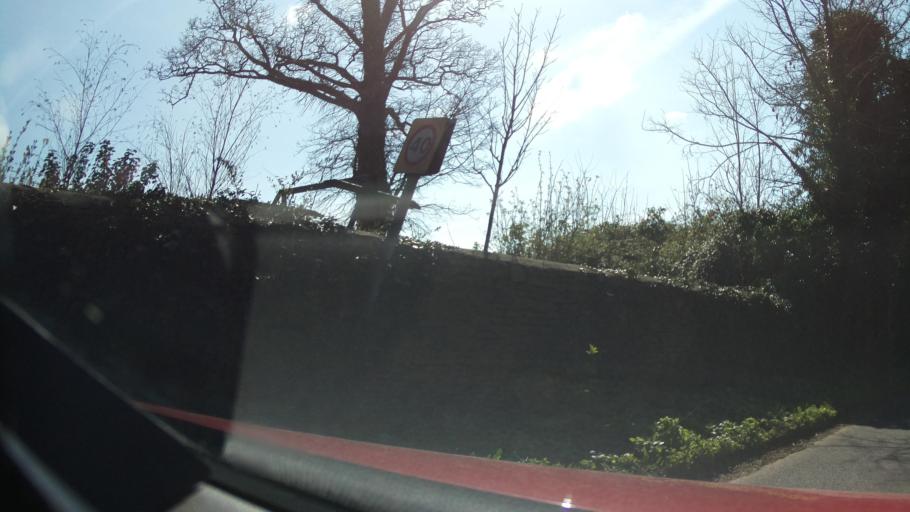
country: GB
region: England
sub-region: Wiltshire
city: Bradford-on-Avon
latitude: 51.3576
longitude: -2.2537
